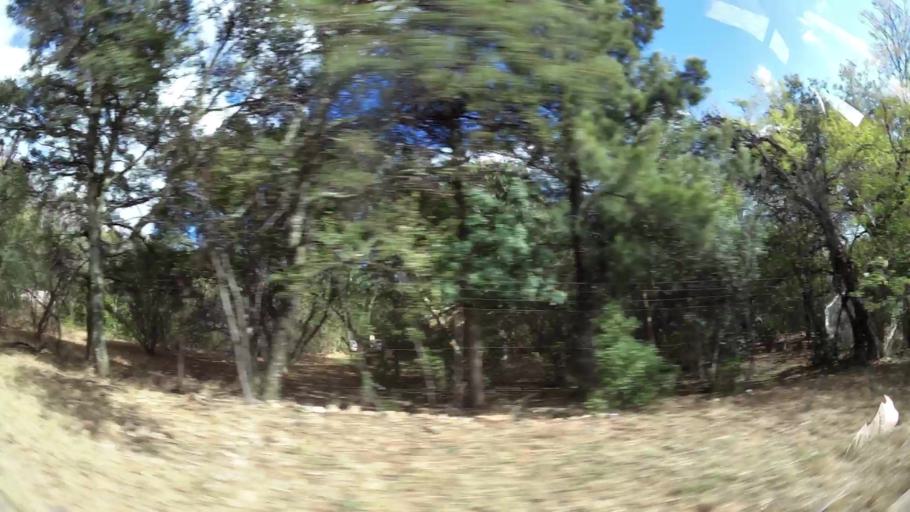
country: ZA
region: Gauteng
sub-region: West Rand District Municipality
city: Muldersdriseloop
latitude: -26.0920
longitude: 27.8523
